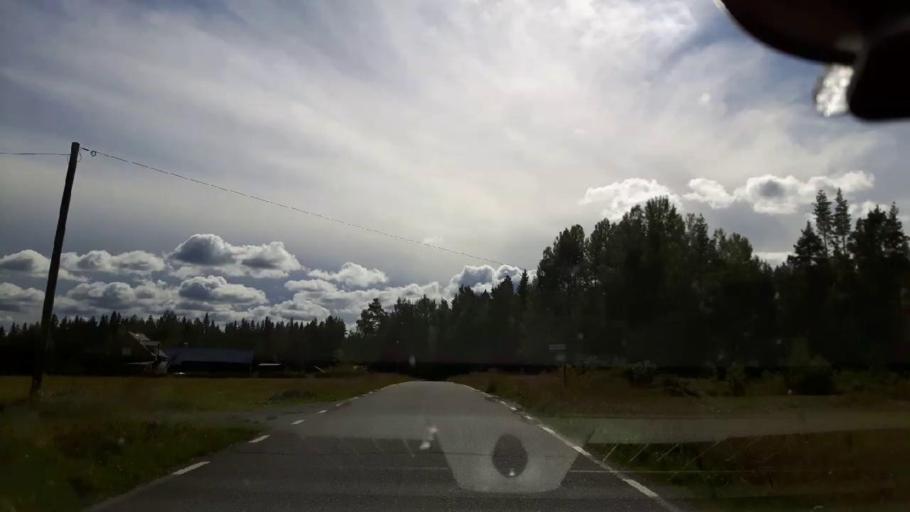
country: SE
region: Jaemtland
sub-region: Braecke Kommun
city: Braecke
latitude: 63.2078
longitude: 15.3517
